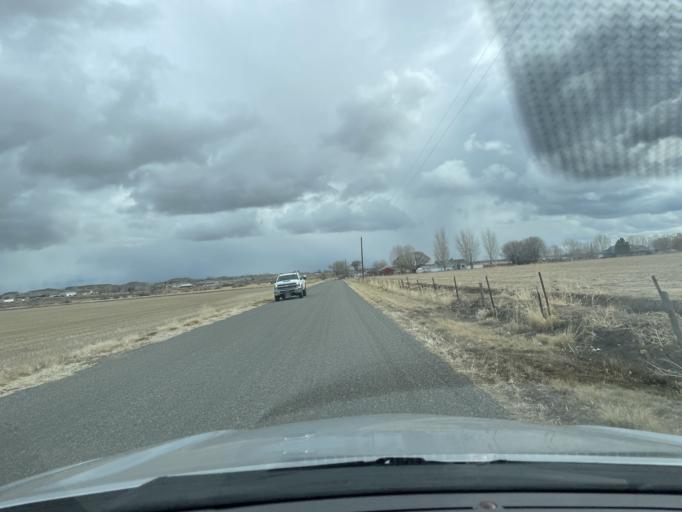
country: US
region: Colorado
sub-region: Mesa County
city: Loma
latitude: 39.1860
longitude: -108.8066
